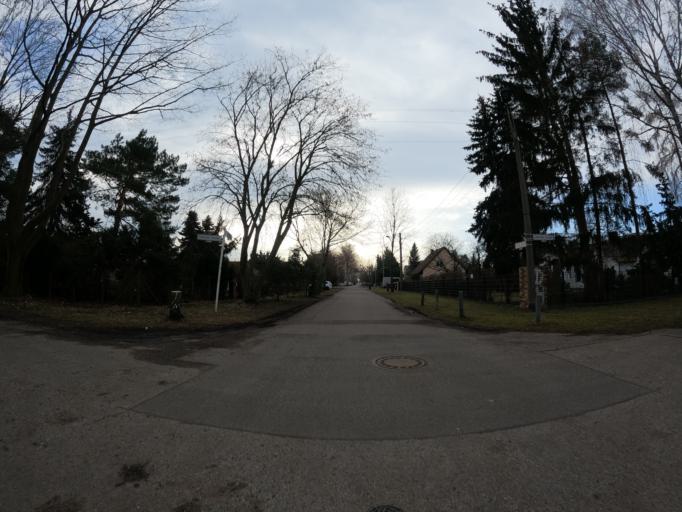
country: DE
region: Brandenburg
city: Hoppegarten
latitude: 52.5252
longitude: 13.6405
